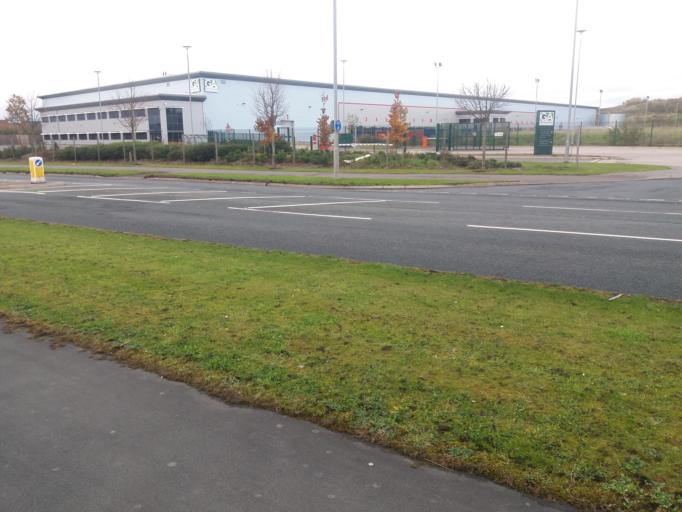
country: GB
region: England
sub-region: Lancashire
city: Euxton
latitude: 53.6737
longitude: -2.6498
